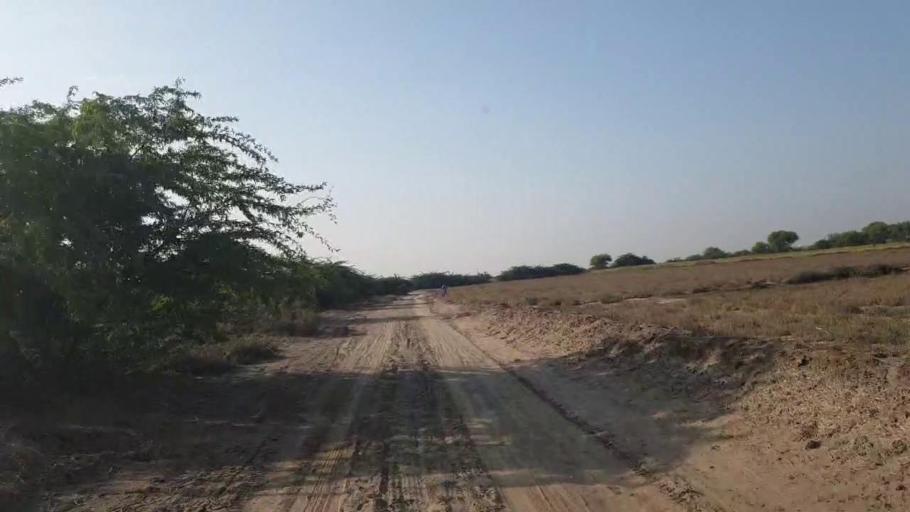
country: PK
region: Sindh
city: Badin
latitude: 24.4559
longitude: 68.7343
